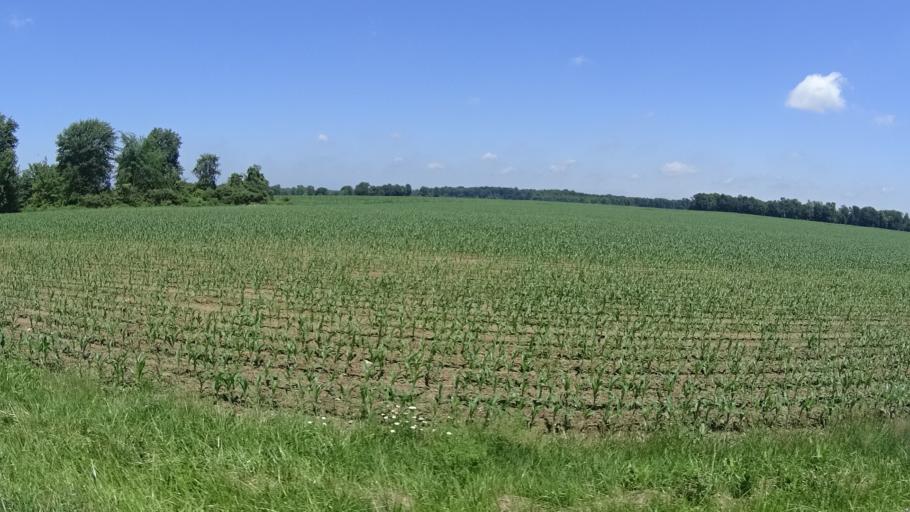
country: US
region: Ohio
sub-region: Huron County
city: Wakeman
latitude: 41.3412
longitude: -82.4228
